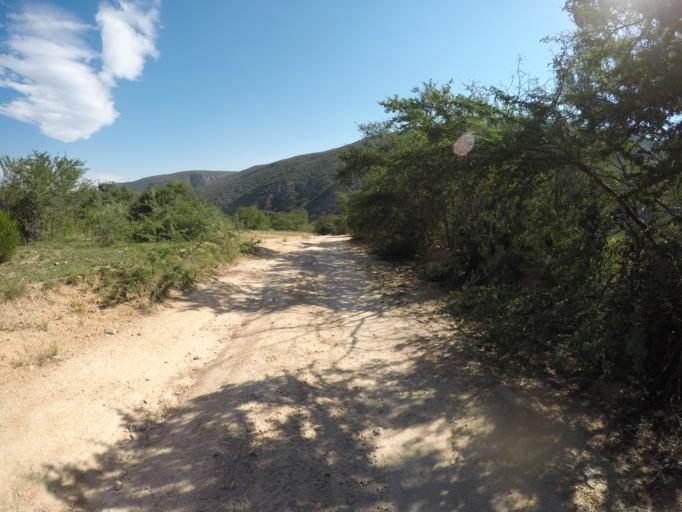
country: ZA
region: Eastern Cape
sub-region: Cacadu District Municipality
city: Kareedouw
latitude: -33.6456
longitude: 24.4607
